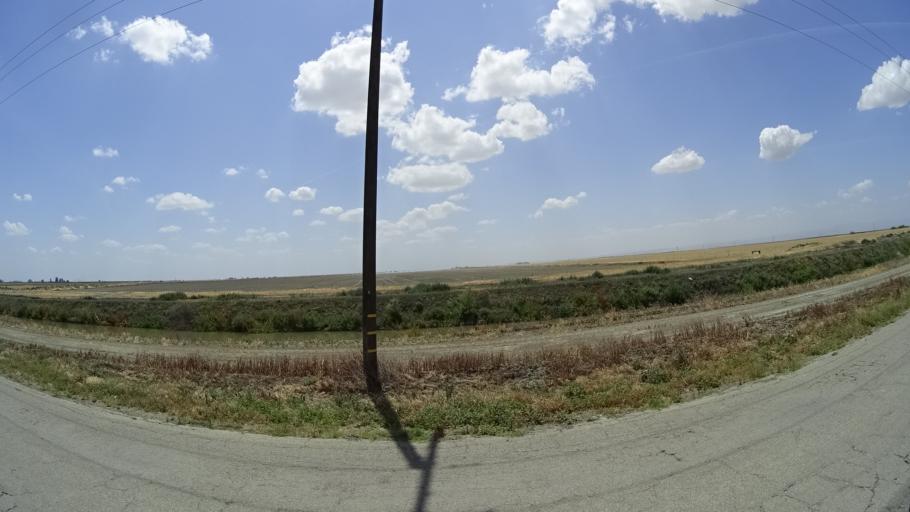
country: US
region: California
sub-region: Kings County
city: Stratford
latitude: 36.1895
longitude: -119.8732
